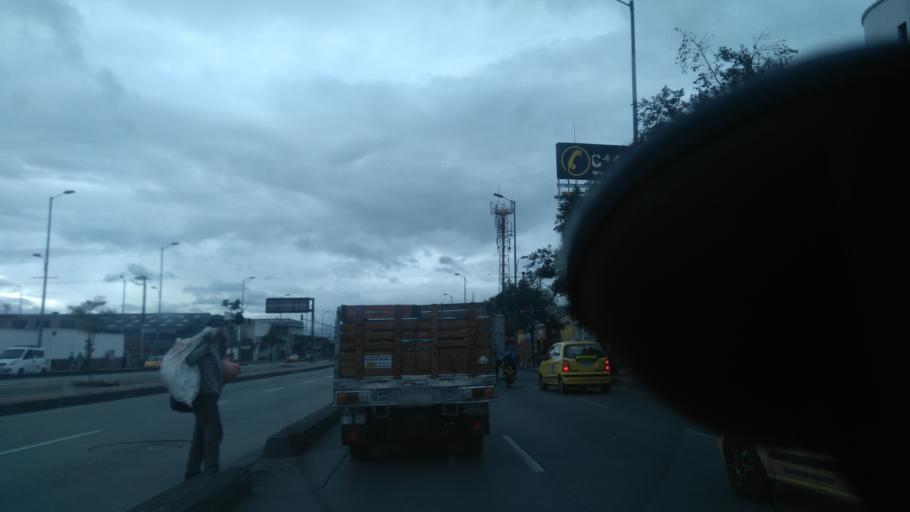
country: CO
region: Bogota D.C.
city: Bogota
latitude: 4.6182
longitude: -74.0961
